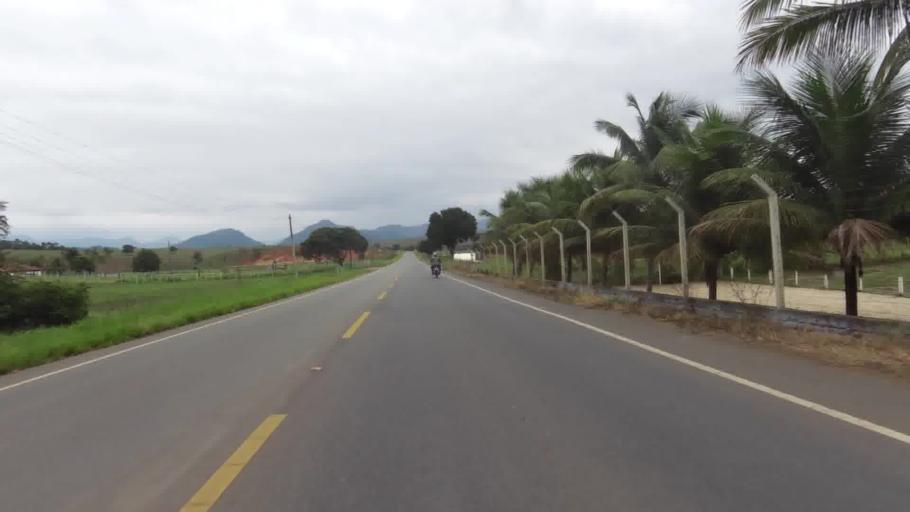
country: BR
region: Espirito Santo
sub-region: Piuma
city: Piuma
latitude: -20.8055
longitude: -40.7427
